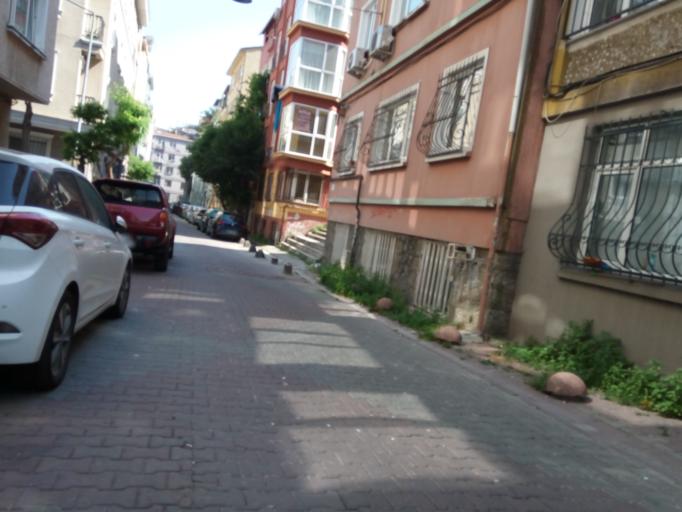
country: TR
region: Istanbul
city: Eminoenue
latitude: 41.0336
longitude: 28.9865
